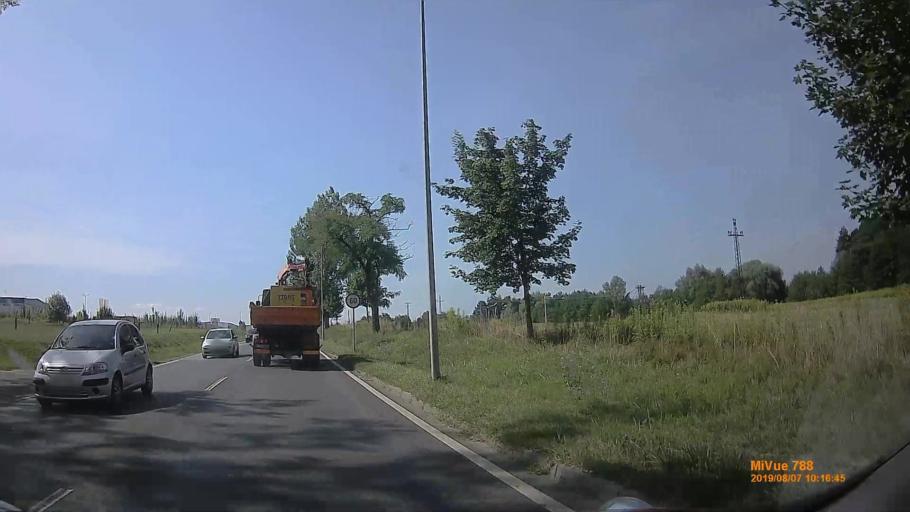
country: HU
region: Veszprem
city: Ajka
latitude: 47.1274
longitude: 17.5455
